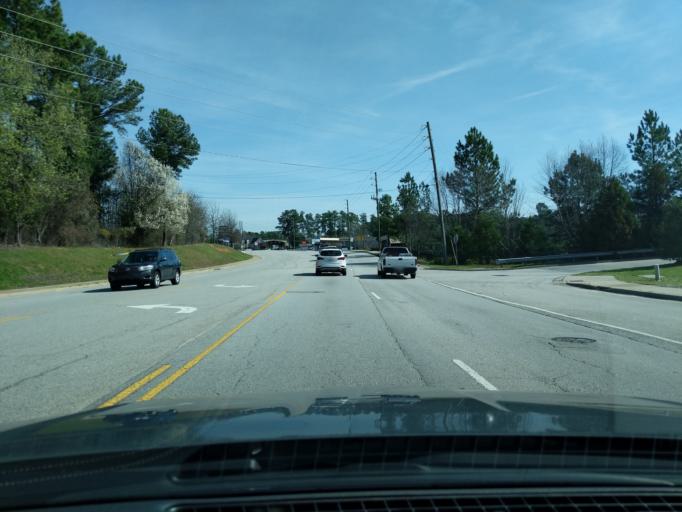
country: US
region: Georgia
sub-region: Columbia County
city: Evans
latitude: 33.5384
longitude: -82.1266
